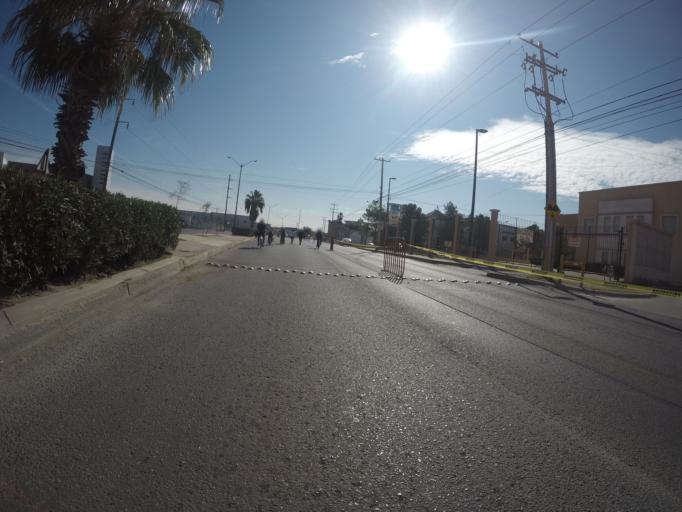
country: MX
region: Chihuahua
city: Ciudad Juarez
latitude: 31.7245
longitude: -106.4017
